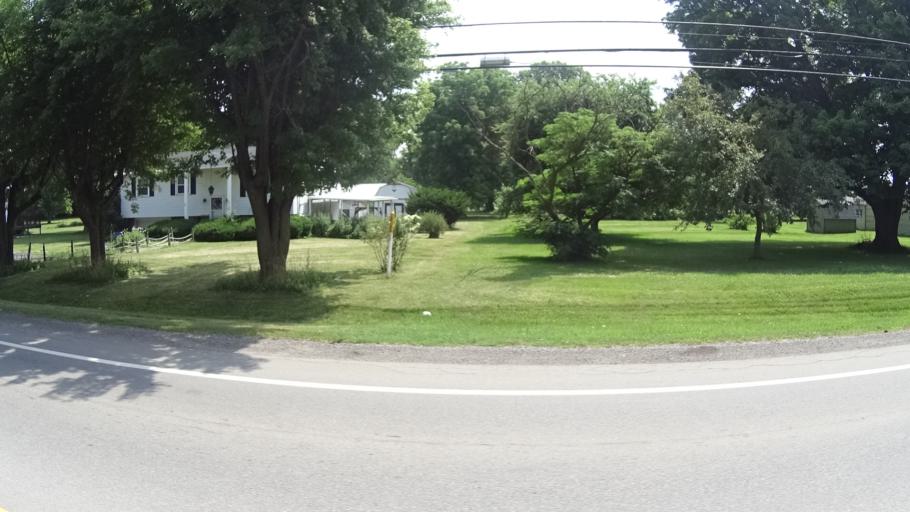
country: US
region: Ohio
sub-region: Lorain County
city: Vermilion
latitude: 41.3697
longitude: -82.3636
